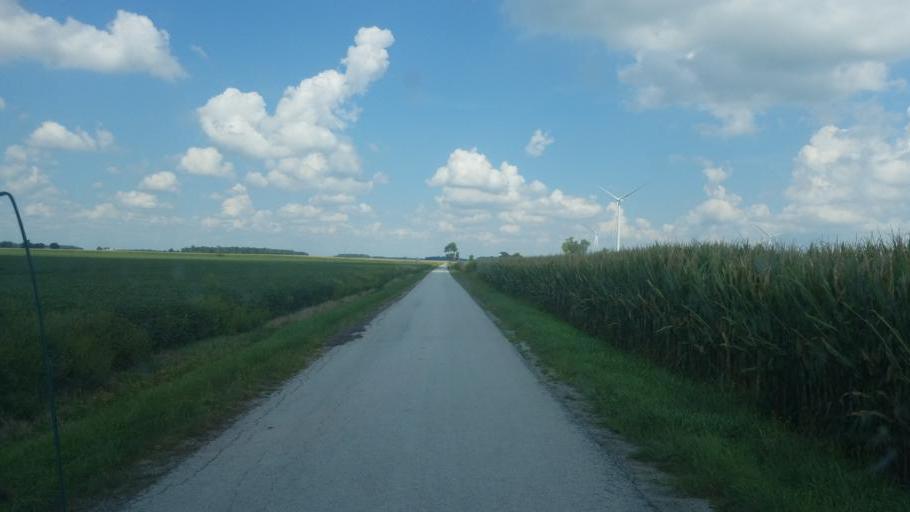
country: US
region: Ohio
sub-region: Hardin County
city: Ada
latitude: 40.7791
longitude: -83.7479
